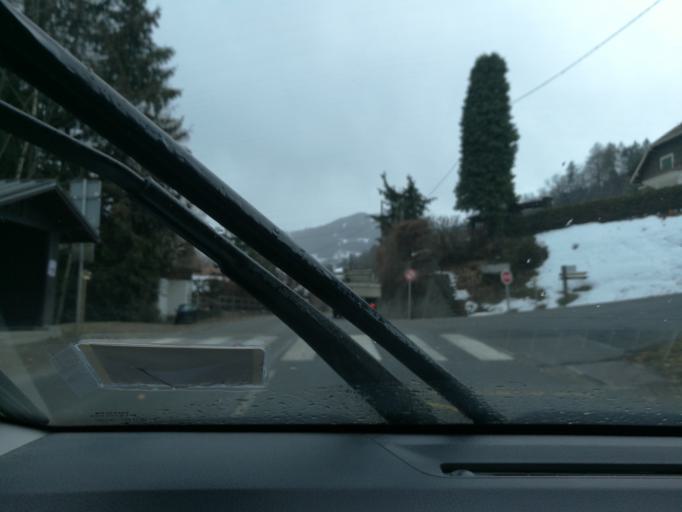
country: FR
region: Rhone-Alpes
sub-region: Departement de la Haute-Savoie
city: Saint-Gervais-les-Bains
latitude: 45.8894
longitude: 6.7017
